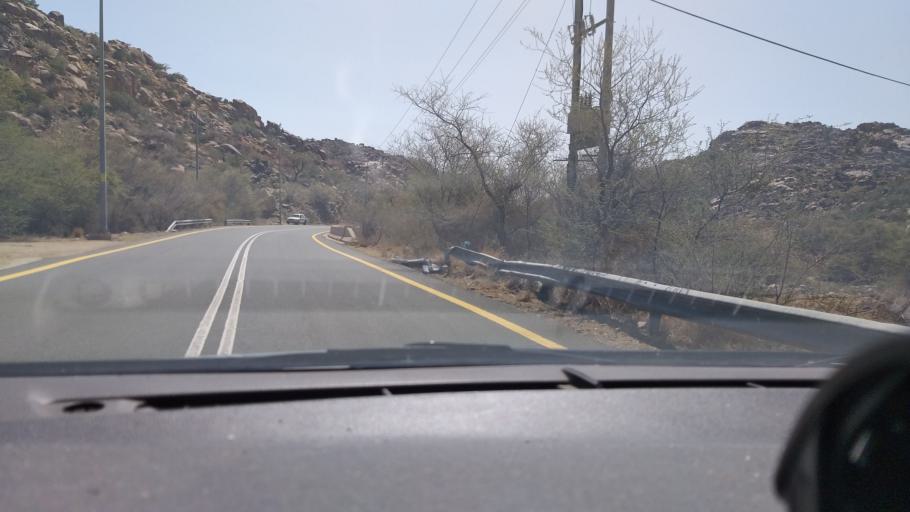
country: SA
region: Makkah
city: Ash Shafa
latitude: 21.0927
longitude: 40.3591
